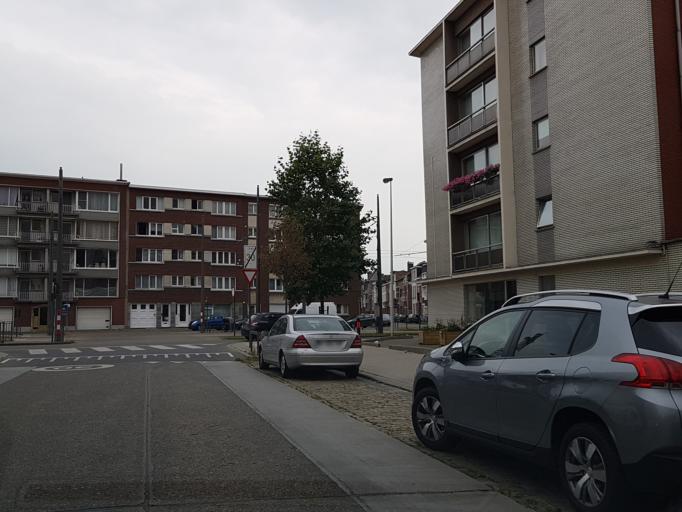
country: BE
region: Flanders
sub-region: Provincie Antwerpen
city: Borsbeek
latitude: 51.2028
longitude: 4.4622
